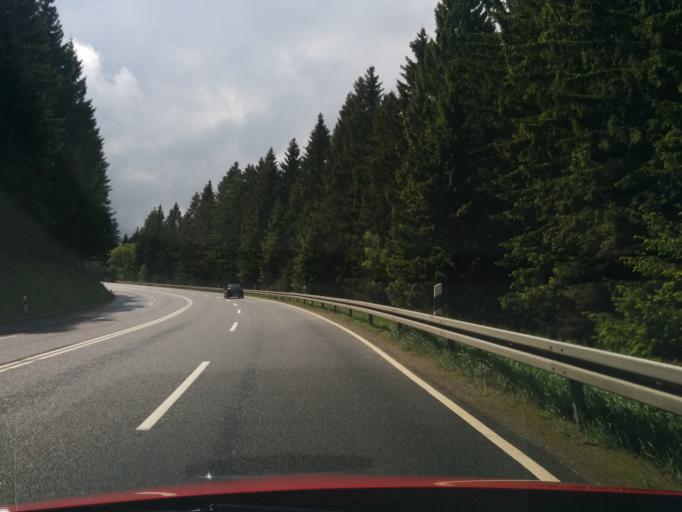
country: DE
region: Lower Saxony
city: Bad Harzburg
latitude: 51.8427
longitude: 10.5295
